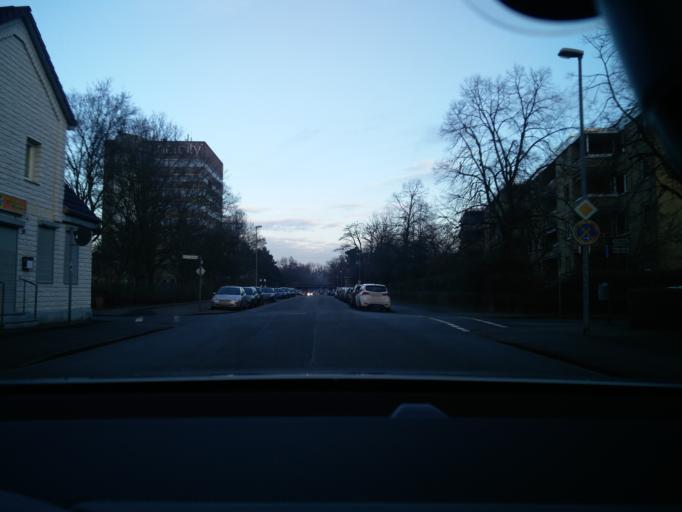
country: DE
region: Lower Saxony
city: Hannover
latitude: 52.3499
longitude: 9.7277
